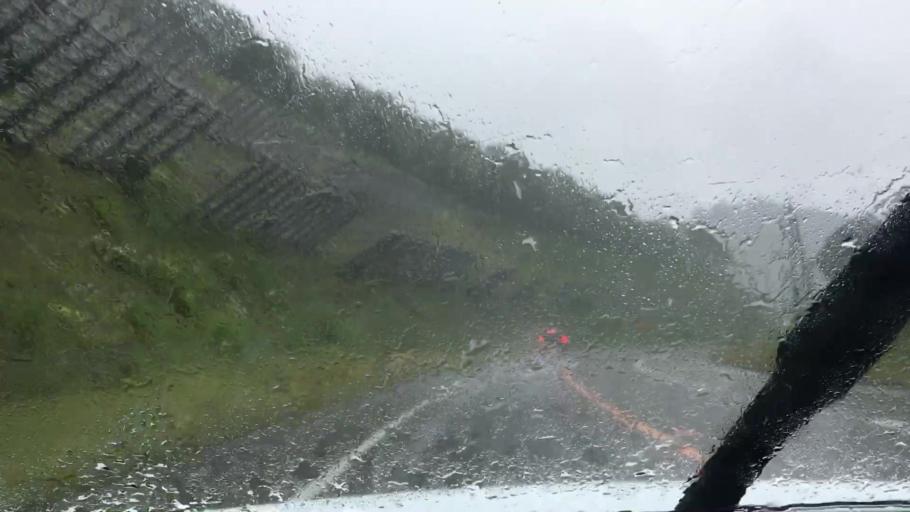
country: JP
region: Hokkaido
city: Sapporo
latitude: 42.8472
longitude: 141.0826
